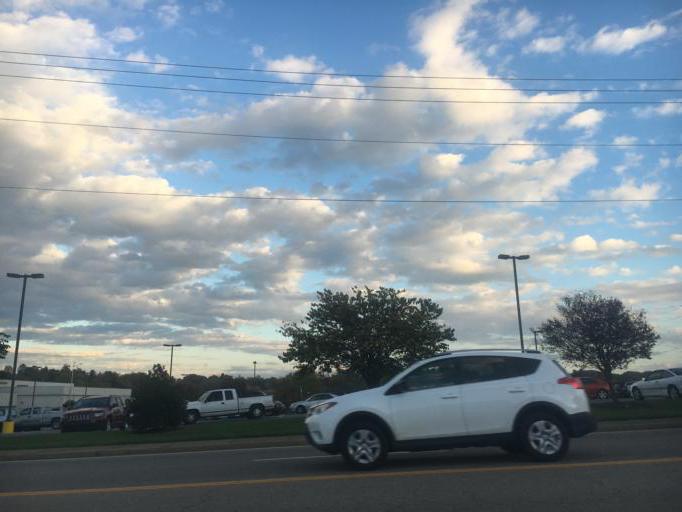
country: US
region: Tennessee
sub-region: Washington County
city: Gray
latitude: 36.4135
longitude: -82.4716
